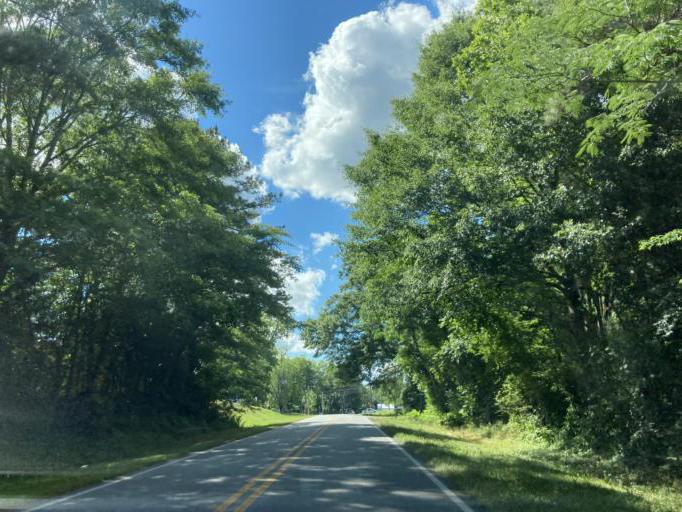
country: US
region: Georgia
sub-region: Jones County
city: Gray
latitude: 32.9971
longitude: -83.5537
